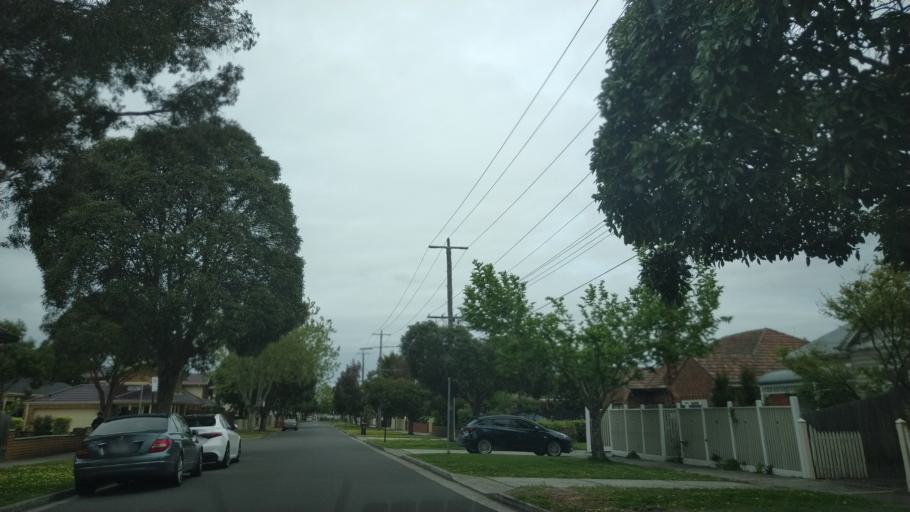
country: AU
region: Victoria
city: Hughesdale
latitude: -37.8953
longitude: 145.0848
